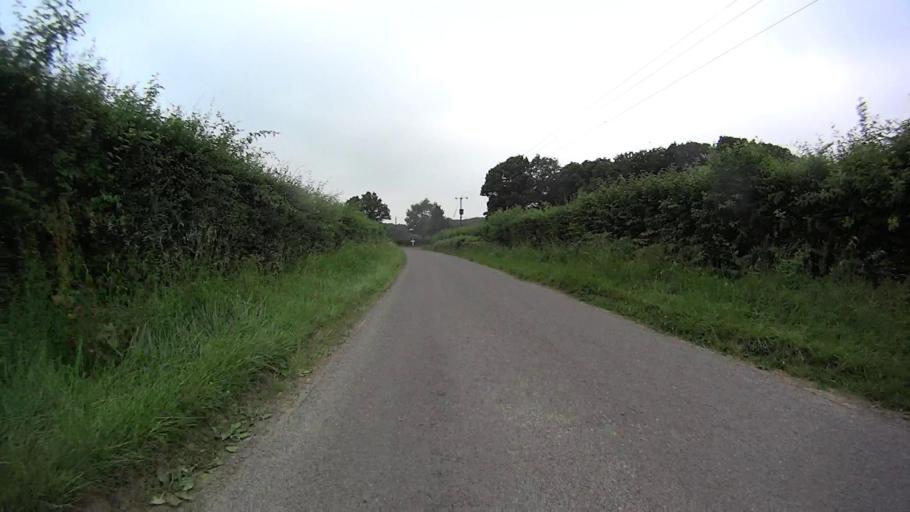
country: GB
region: England
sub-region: West Sussex
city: Bewbush
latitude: 51.1007
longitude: -0.2768
